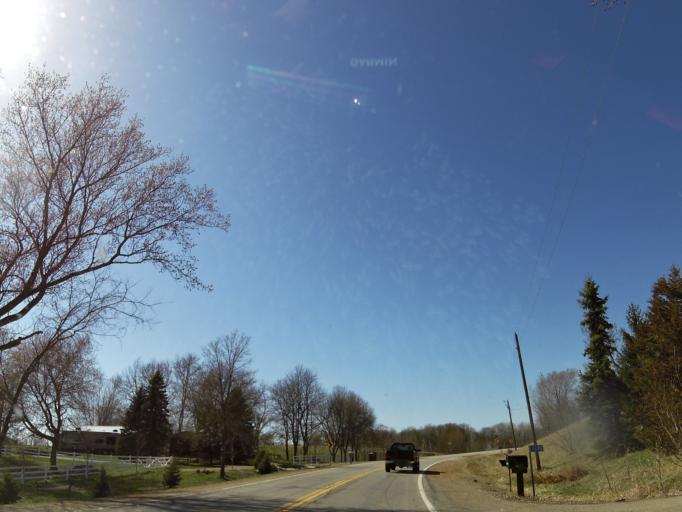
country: US
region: Minnesota
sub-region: Scott County
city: Prior Lake
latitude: 44.6684
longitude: -93.3658
